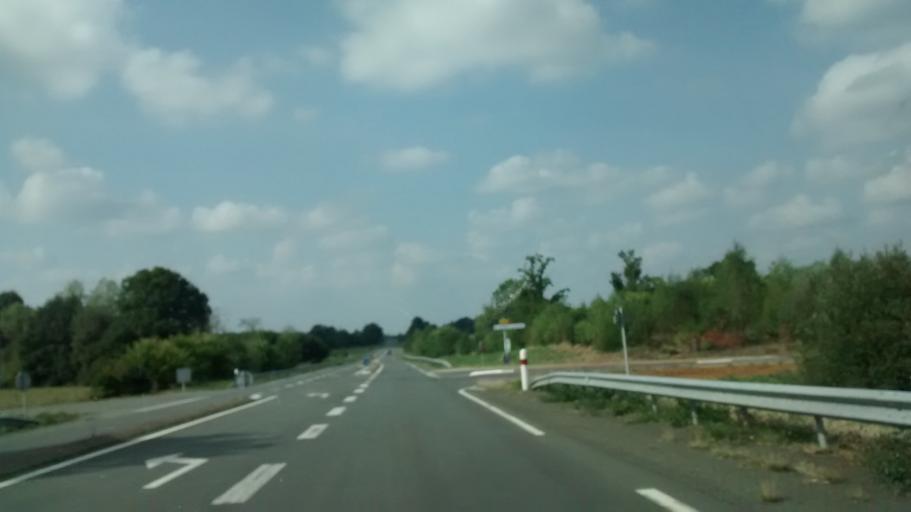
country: FR
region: Brittany
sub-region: Departement d'Ille-et-Vilaine
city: Livre-sur-Changeon
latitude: 48.2404
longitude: -1.3656
